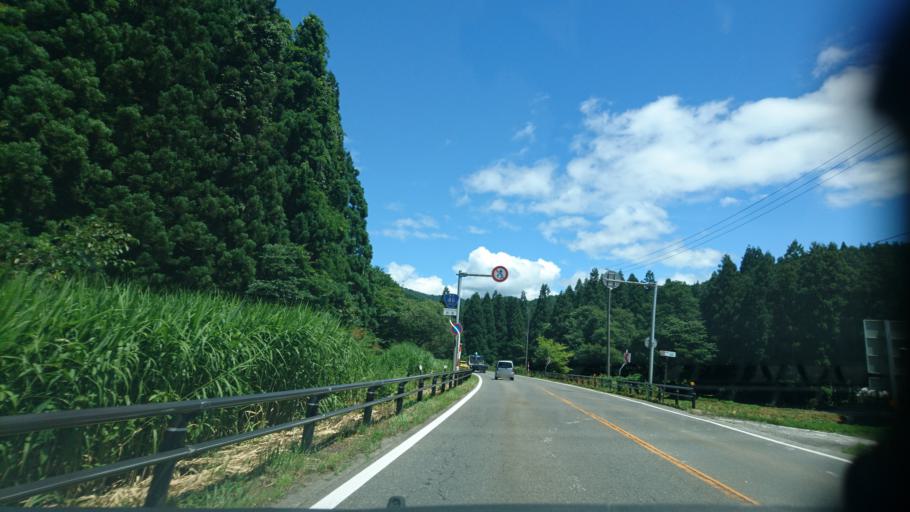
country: JP
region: Akita
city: Kakunodatemachi
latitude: 39.6542
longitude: 140.6721
